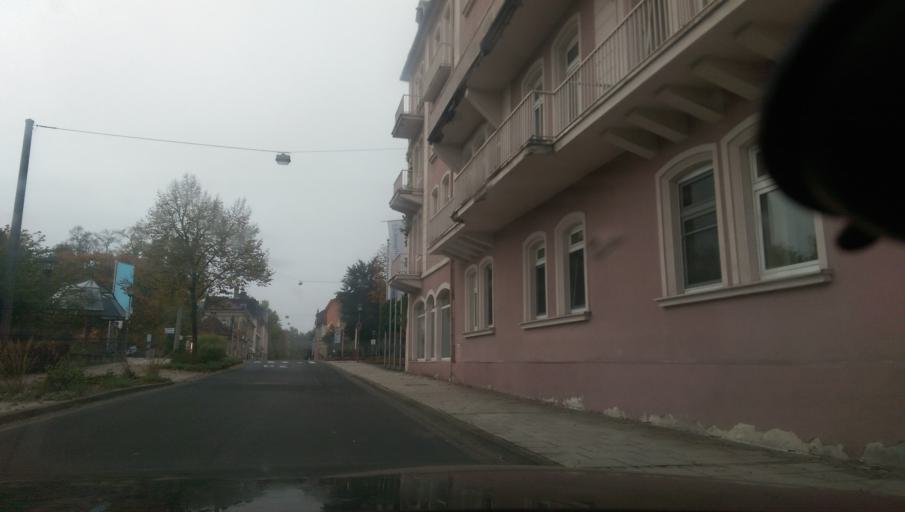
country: DE
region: Bavaria
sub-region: Regierungsbezirk Unterfranken
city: Bad Kissingen
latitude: 50.1984
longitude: 10.0720
